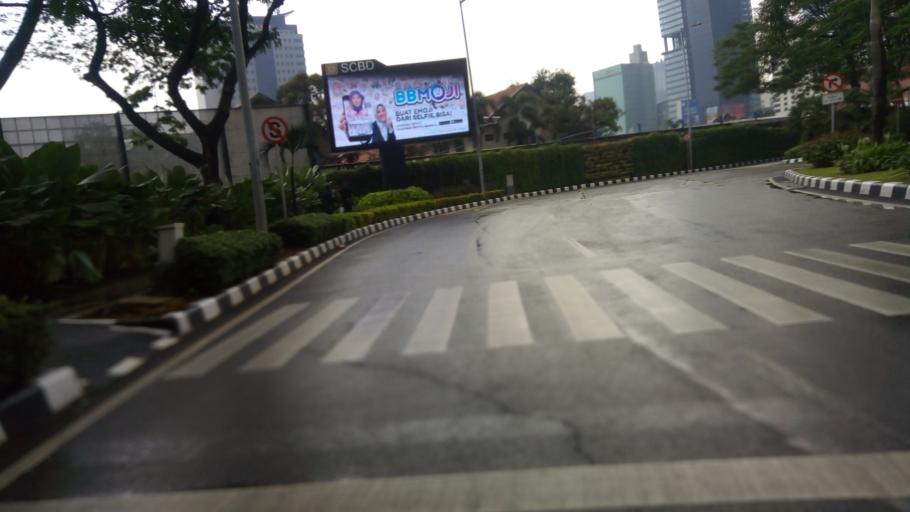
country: ID
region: Jakarta Raya
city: Jakarta
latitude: -6.2252
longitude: 106.8128
